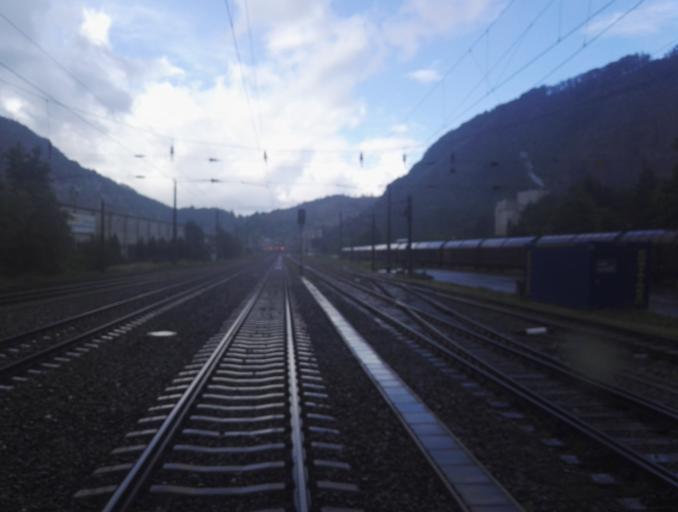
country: AT
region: Styria
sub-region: Politischer Bezirk Graz-Umgebung
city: Peggau
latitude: 47.2087
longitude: 15.3429
